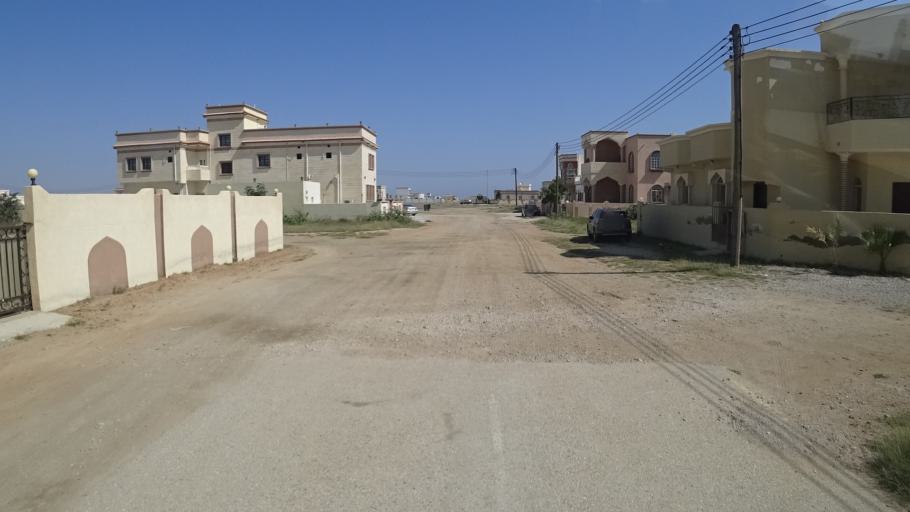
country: OM
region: Zufar
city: Salalah
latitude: 16.9826
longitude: 54.7094
